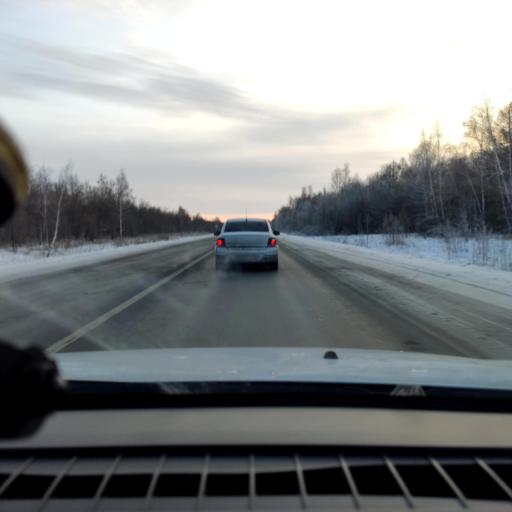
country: RU
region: Samara
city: Chapayevsk
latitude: 52.9938
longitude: 49.8217
